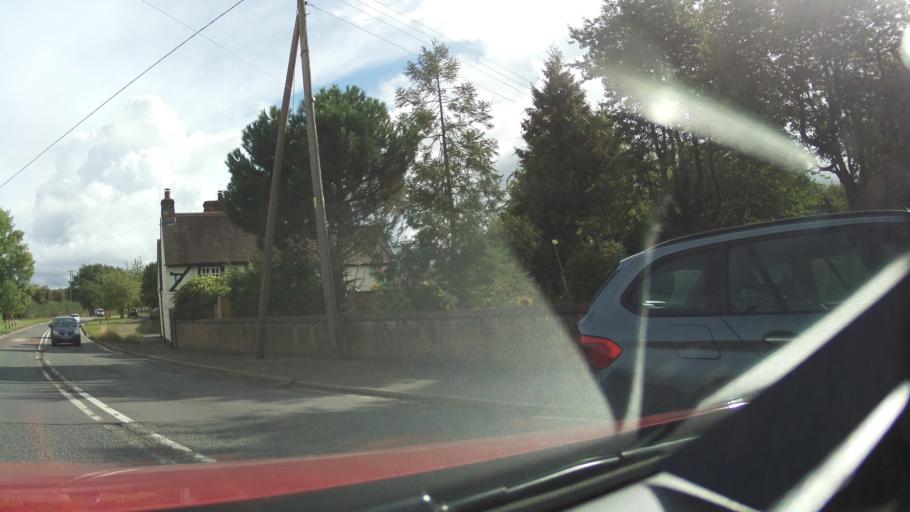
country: GB
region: England
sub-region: Telford and Wrekin
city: Madeley
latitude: 52.6004
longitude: -2.4024
